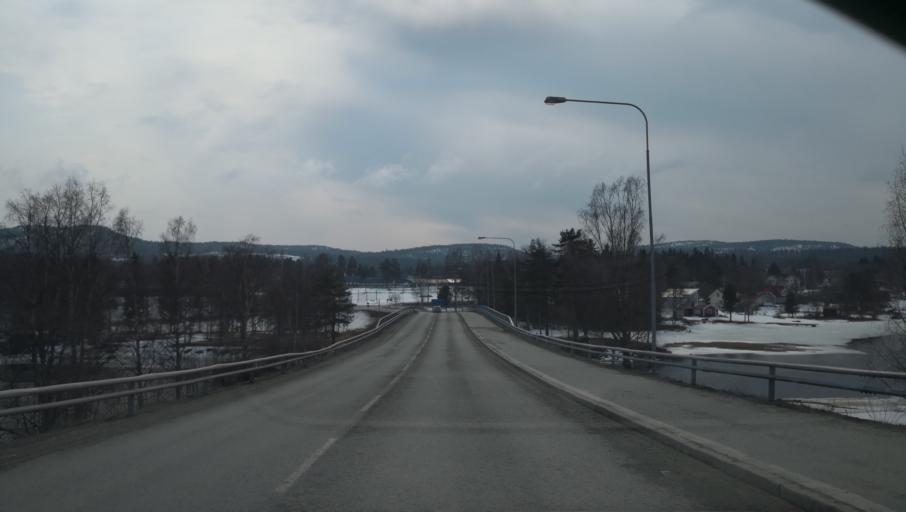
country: SE
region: Vaesternorrland
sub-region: OErnskoeldsviks Kommun
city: Ornskoldsvik
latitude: 63.2919
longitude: 18.6109
